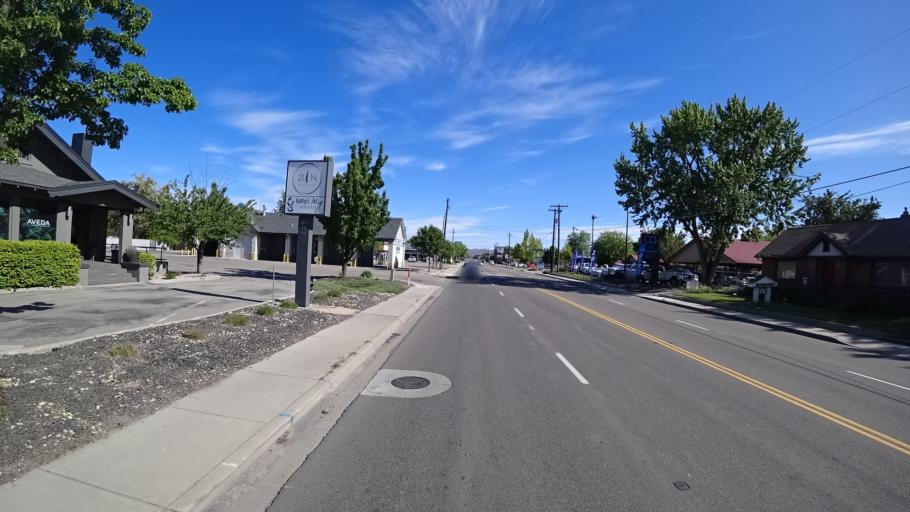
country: US
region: Idaho
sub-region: Ada County
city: Garden City
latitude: 43.6050
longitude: -116.2436
